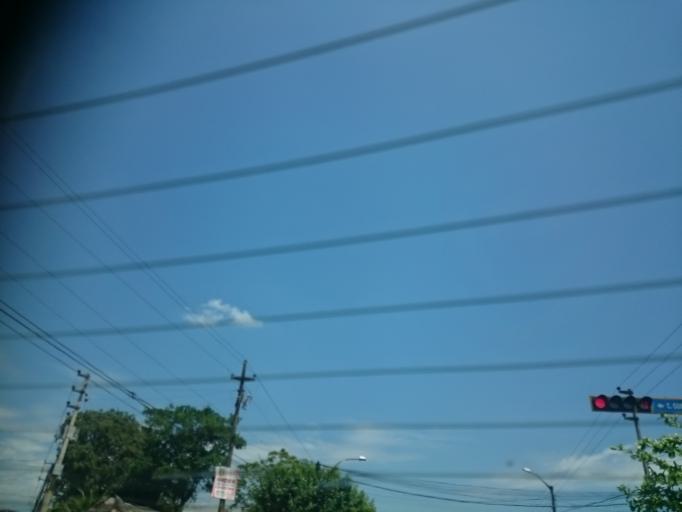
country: PE
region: Loreto
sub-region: Provincia de Maynas
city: Iquitos
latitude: -3.7672
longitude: -73.2736
